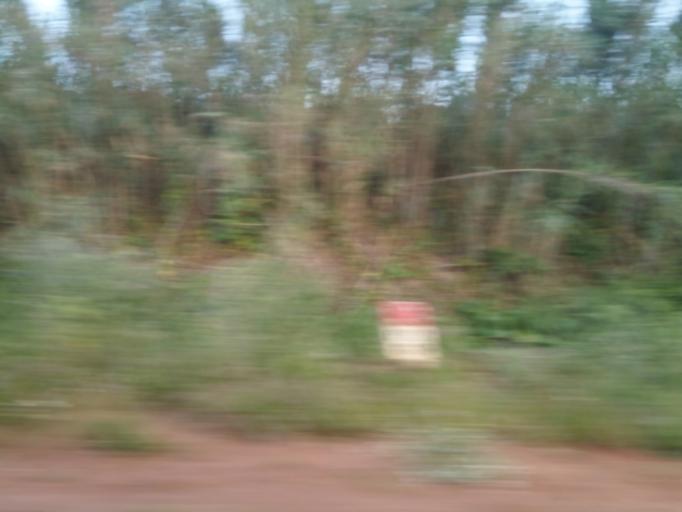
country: DZ
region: Tipaza
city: Bou Ismail
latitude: 36.6114
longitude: 2.6296
